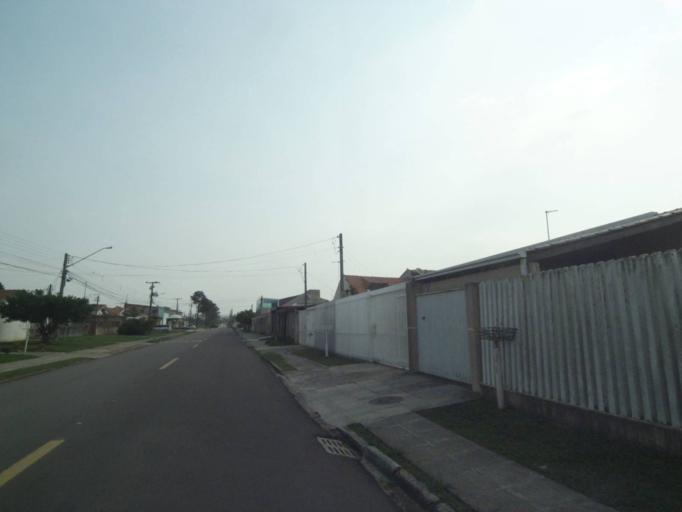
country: BR
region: Parana
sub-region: Sao Jose Dos Pinhais
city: Sao Jose dos Pinhais
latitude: -25.5277
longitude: -49.2290
